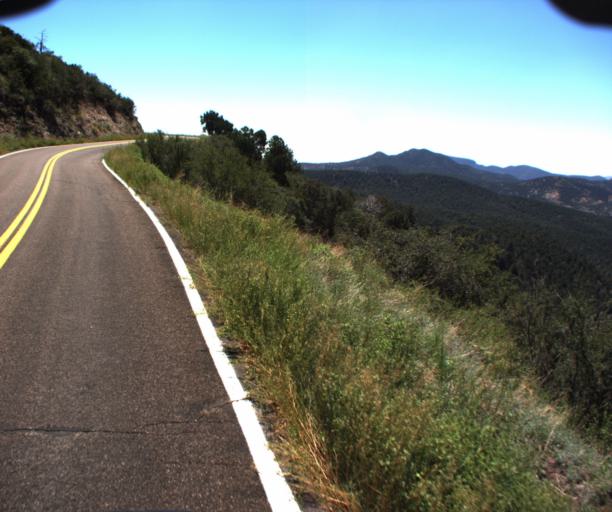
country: US
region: Arizona
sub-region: Greenlee County
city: Morenci
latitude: 33.2200
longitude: -109.3856
